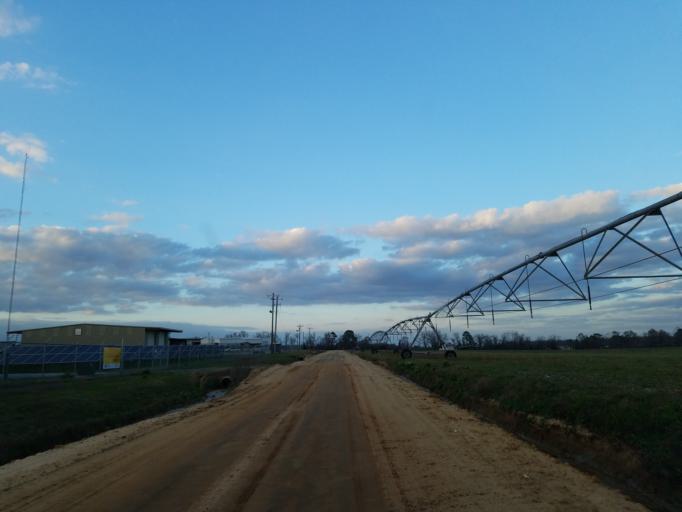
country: US
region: Georgia
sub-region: Dooly County
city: Vienna
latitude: 32.0892
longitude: -83.7523
